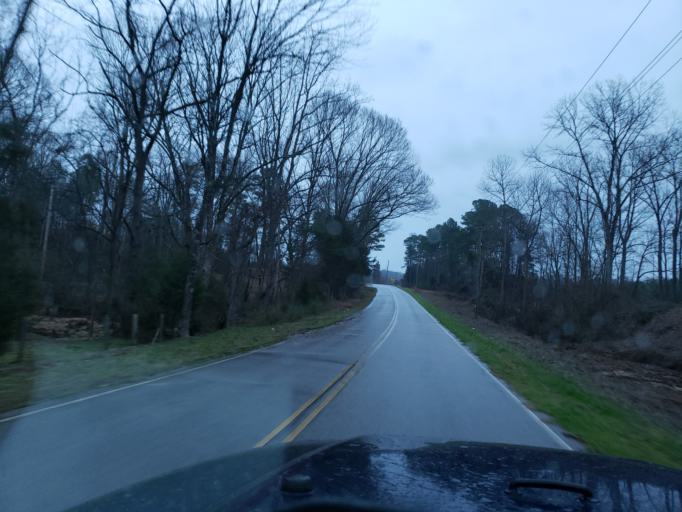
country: US
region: South Carolina
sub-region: Cherokee County
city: Blacksburg
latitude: 35.1563
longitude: -81.4562
